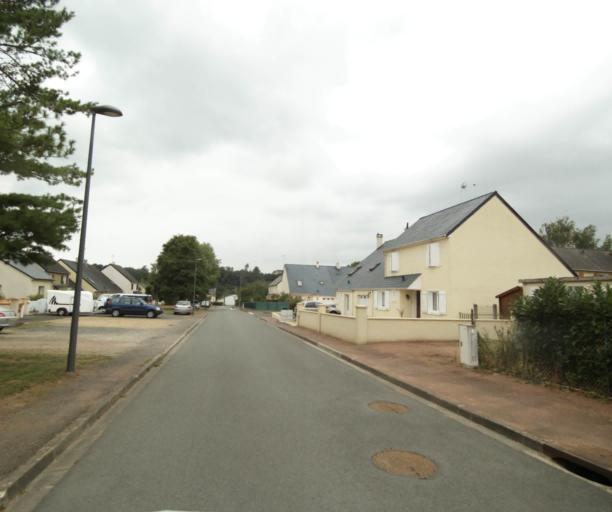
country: FR
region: Pays de la Loire
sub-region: Departement de la Sarthe
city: Sable-sur-Sarthe
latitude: 47.8414
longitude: -0.3195
